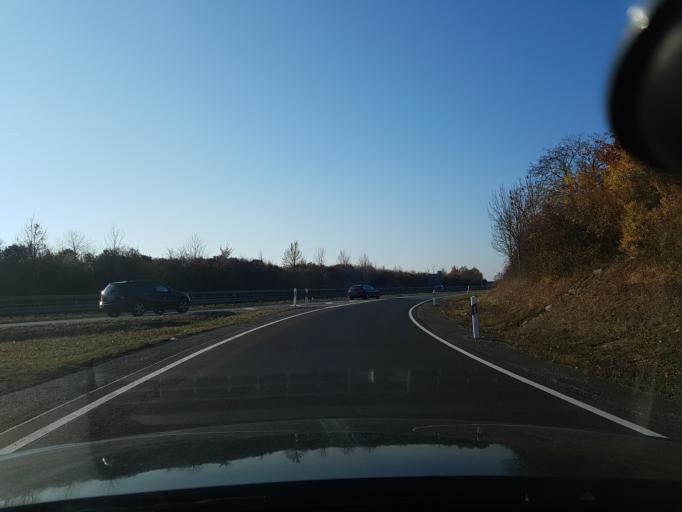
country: DE
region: Bavaria
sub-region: Regierungsbezirk Unterfranken
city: Estenfeld
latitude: 49.8393
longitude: 9.9999
